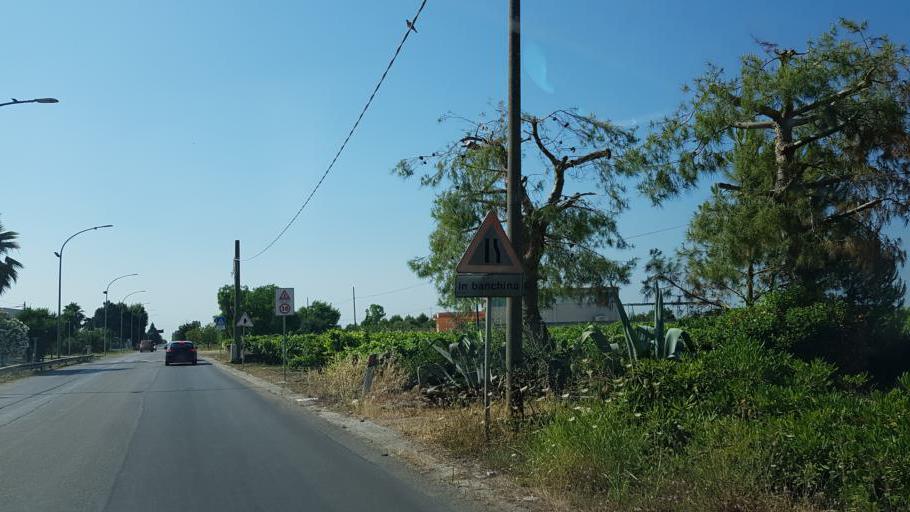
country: IT
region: Apulia
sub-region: Provincia di Brindisi
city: San Donaci
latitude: 40.4409
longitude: 17.9297
